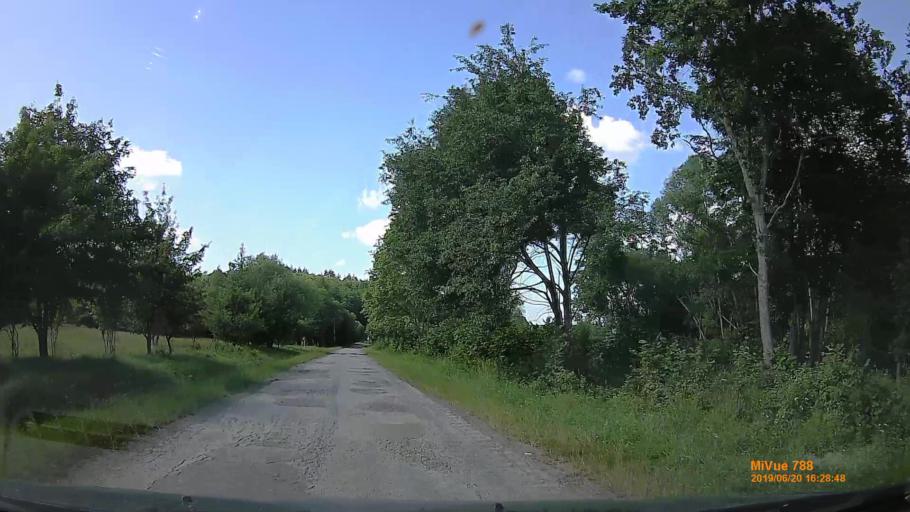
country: HU
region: Baranya
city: Buekkoesd
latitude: 46.1570
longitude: 18.0577
